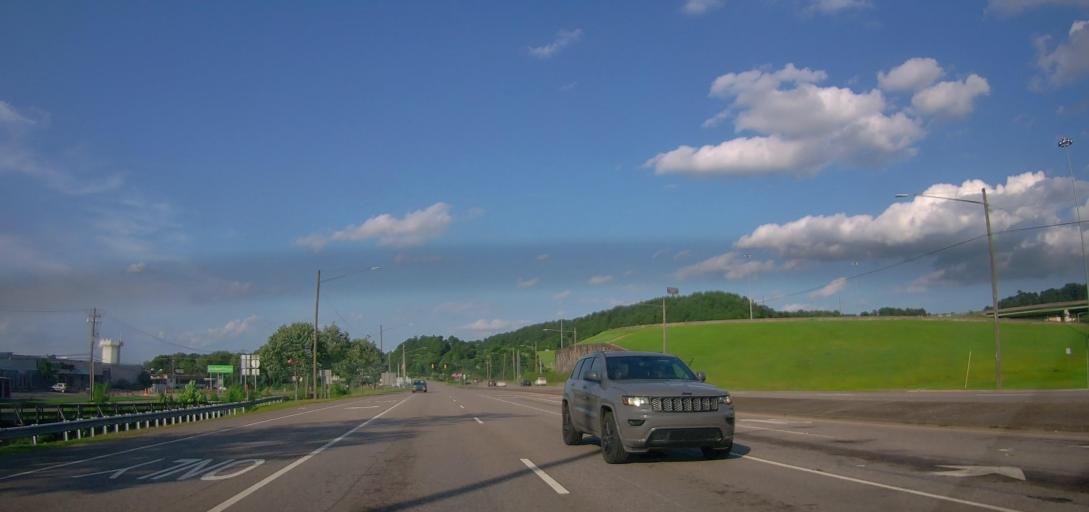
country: US
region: Alabama
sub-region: Jefferson County
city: Irondale
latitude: 33.5347
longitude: -86.7001
